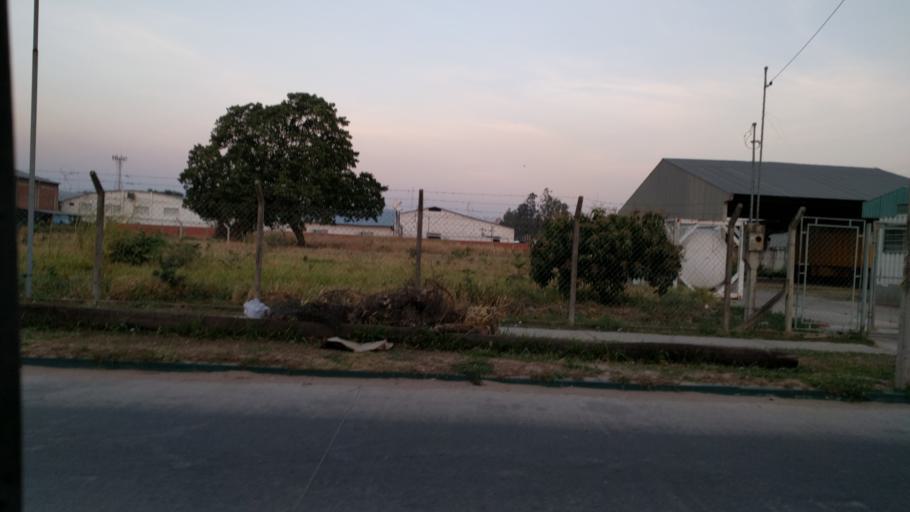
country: BO
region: Santa Cruz
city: Santa Cruz de la Sierra
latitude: -17.7618
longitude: -63.1465
